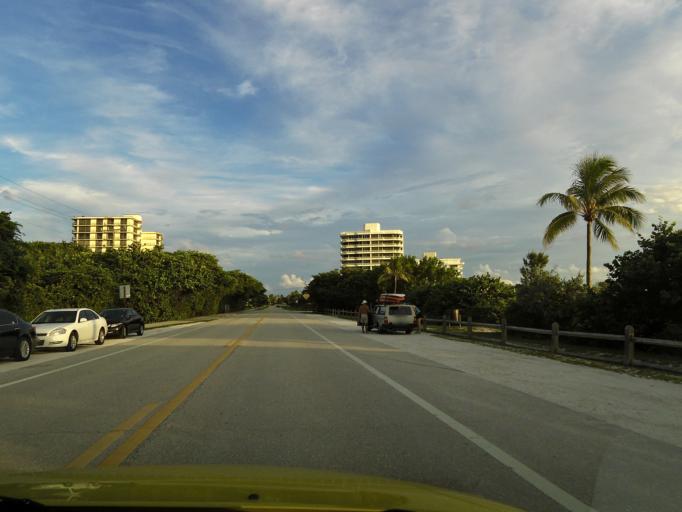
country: US
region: Florida
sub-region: Palm Beach County
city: Jupiter
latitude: 26.9576
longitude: -80.0776
